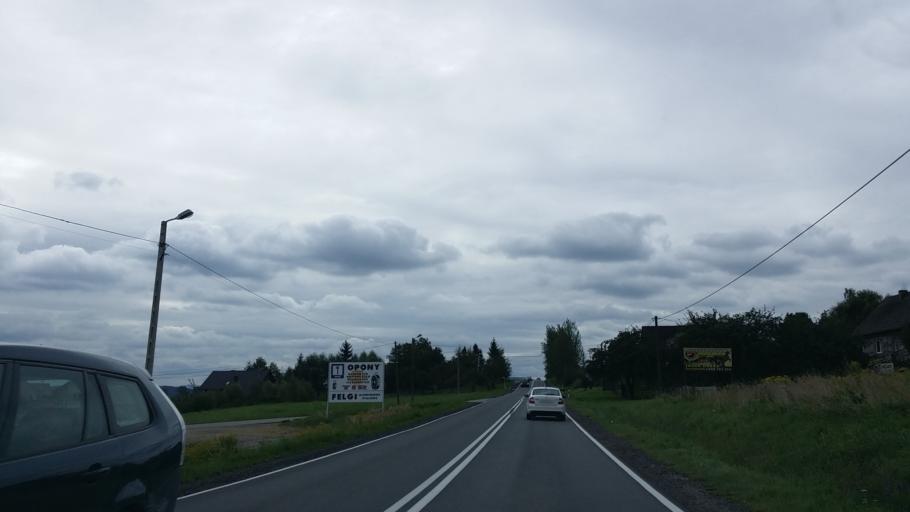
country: PL
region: Lesser Poland Voivodeship
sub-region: Powiat wadowicki
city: Radocza
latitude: 49.9262
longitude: 19.4757
